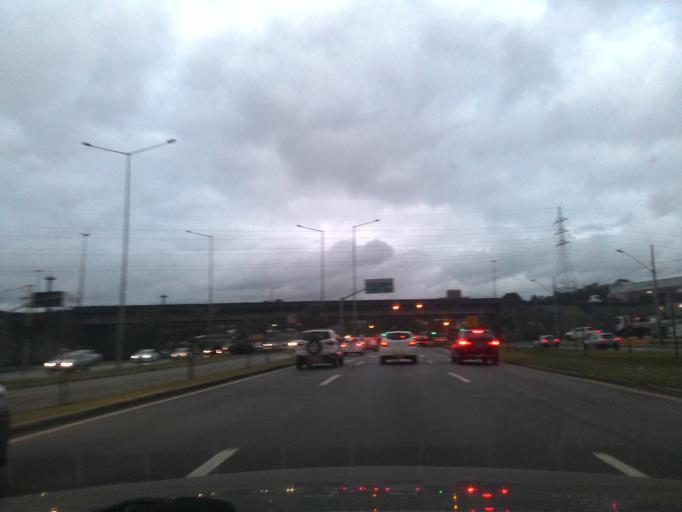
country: BR
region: Parana
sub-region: Curitiba
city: Curitiba
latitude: -25.4536
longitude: -49.2442
